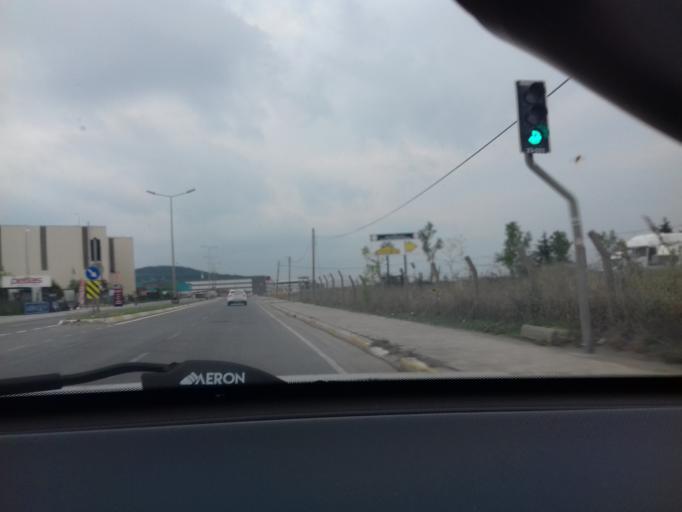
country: TR
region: Istanbul
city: Icmeler
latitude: 40.8893
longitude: 29.3532
